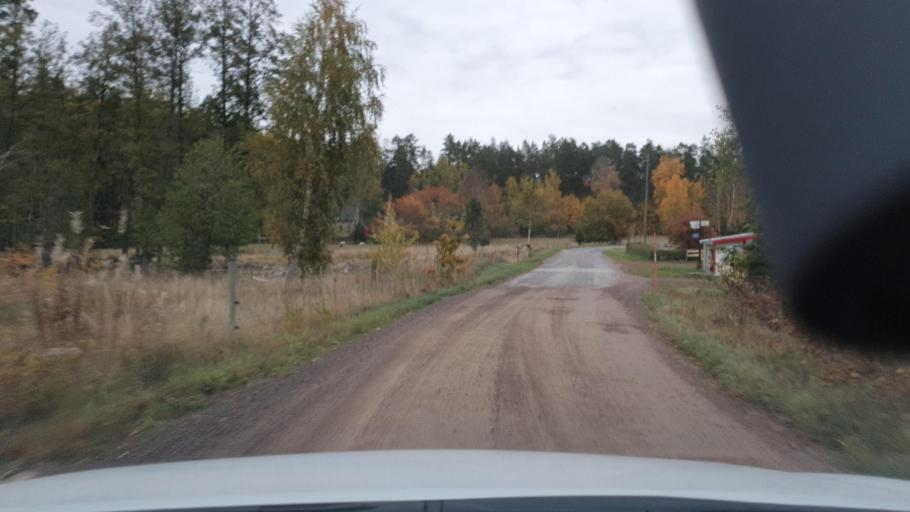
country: SE
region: Kalmar
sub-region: Hultsfreds Kommun
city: Malilla
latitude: 57.3340
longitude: 15.8165
